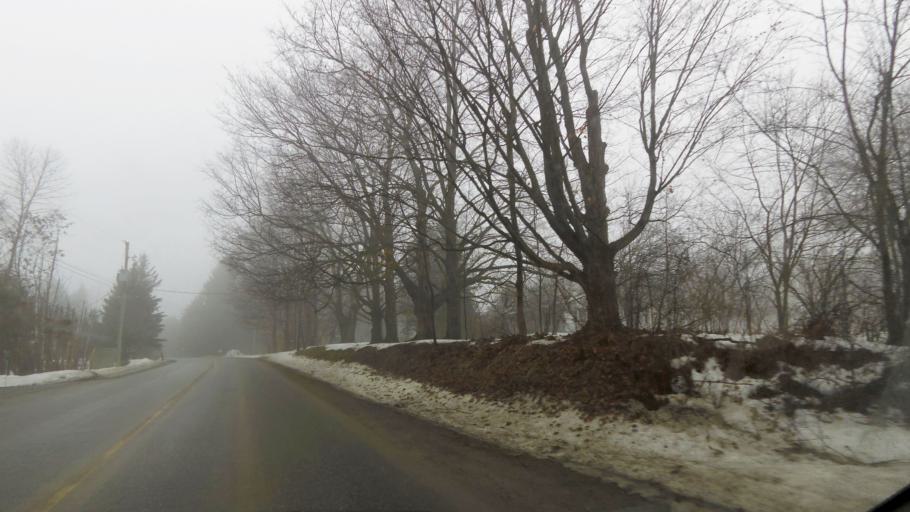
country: CA
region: Ontario
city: Brampton
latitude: 43.8649
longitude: -79.8229
